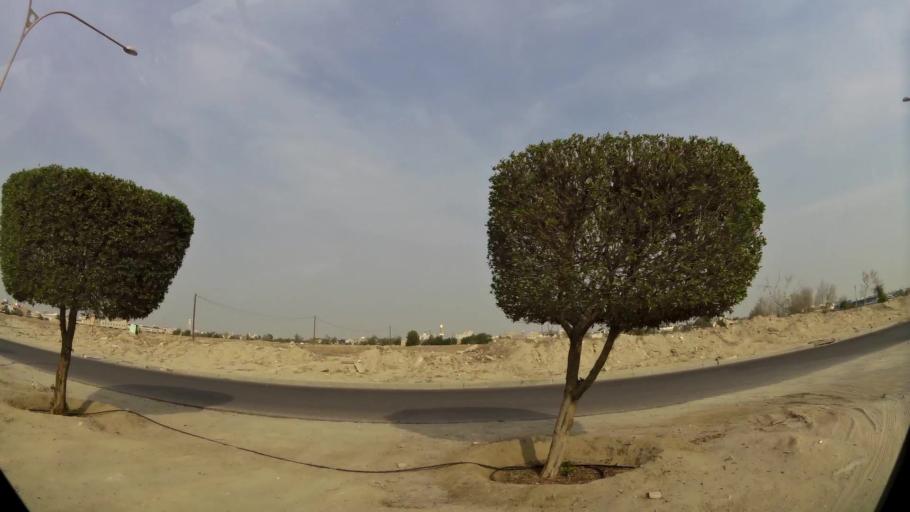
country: KW
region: Al Farwaniyah
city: Janub as Surrah
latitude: 29.2741
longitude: 47.9789
